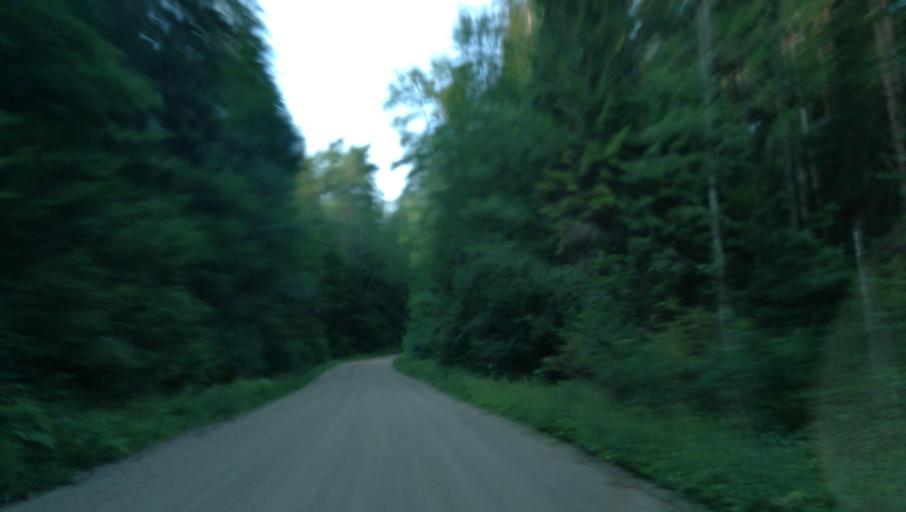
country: LV
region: Cesu Rajons
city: Cesis
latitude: 57.3468
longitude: 25.1879
